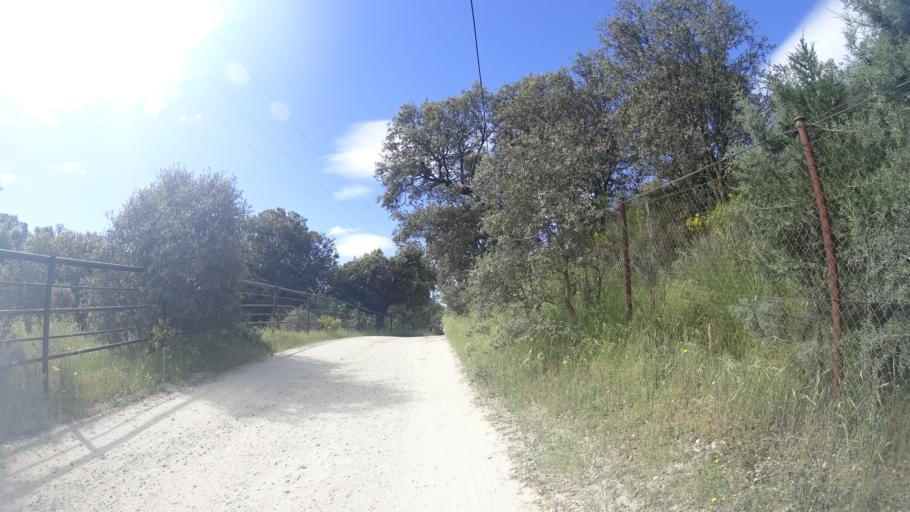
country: ES
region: Madrid
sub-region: Provincia de Madrid
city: Brunete
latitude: 40.4167
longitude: -3.9502
